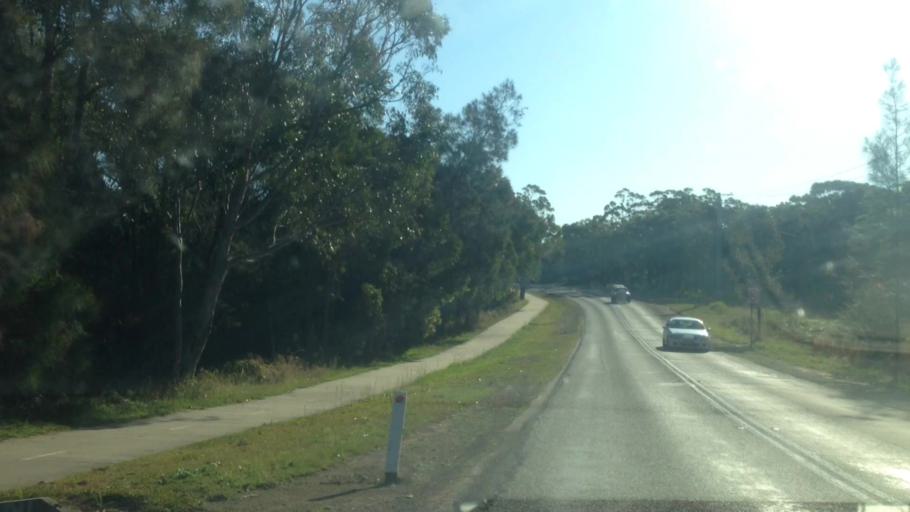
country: AU
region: New South Wales
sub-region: Lake Macquarie Shire
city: Dora Creek
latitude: -33.1083
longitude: 151.5375
